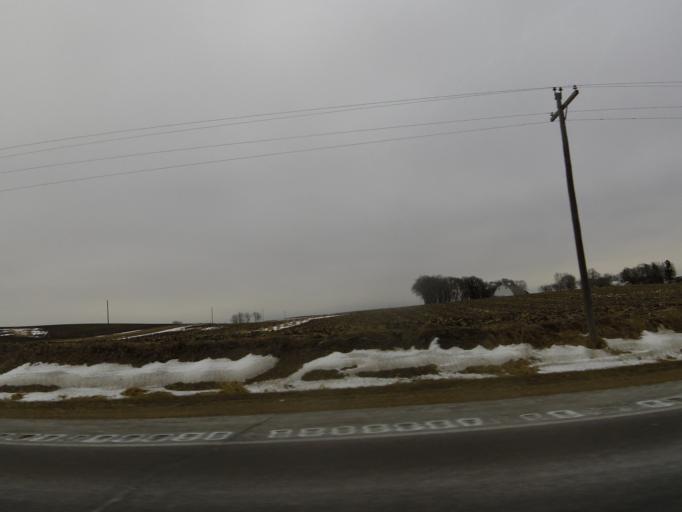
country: US
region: Minnesota
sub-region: Carver County
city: Carver
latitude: 44.7761
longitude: -93.6693
